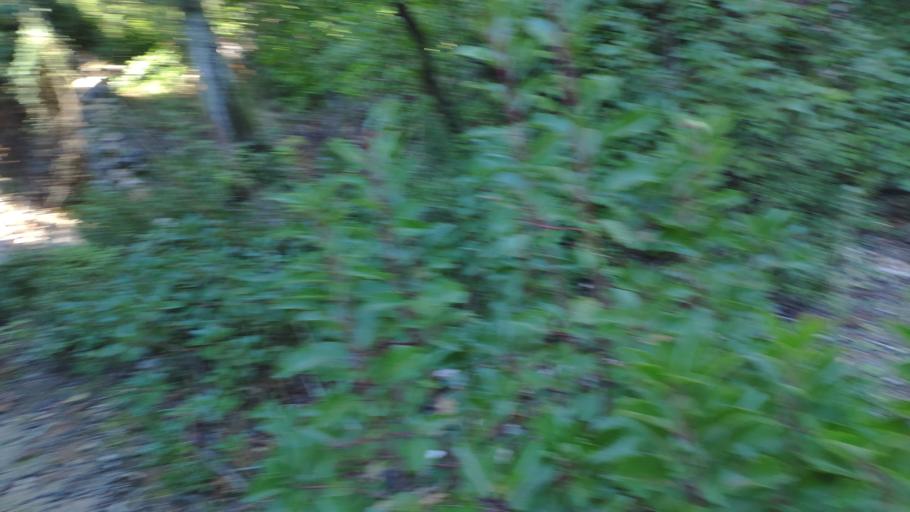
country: GR
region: Attica
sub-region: Nomarchia Anatolikis Attikis
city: Varybobi
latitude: 38.1646
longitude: 23.7933
